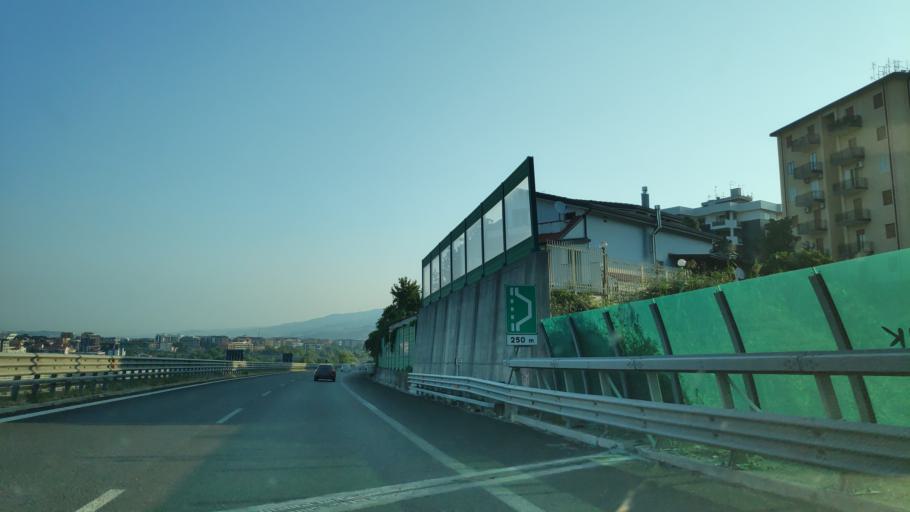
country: IT
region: Calabria
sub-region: Provincia di Cosenza
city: Cosenza
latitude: 39.3111
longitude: 16.2390
